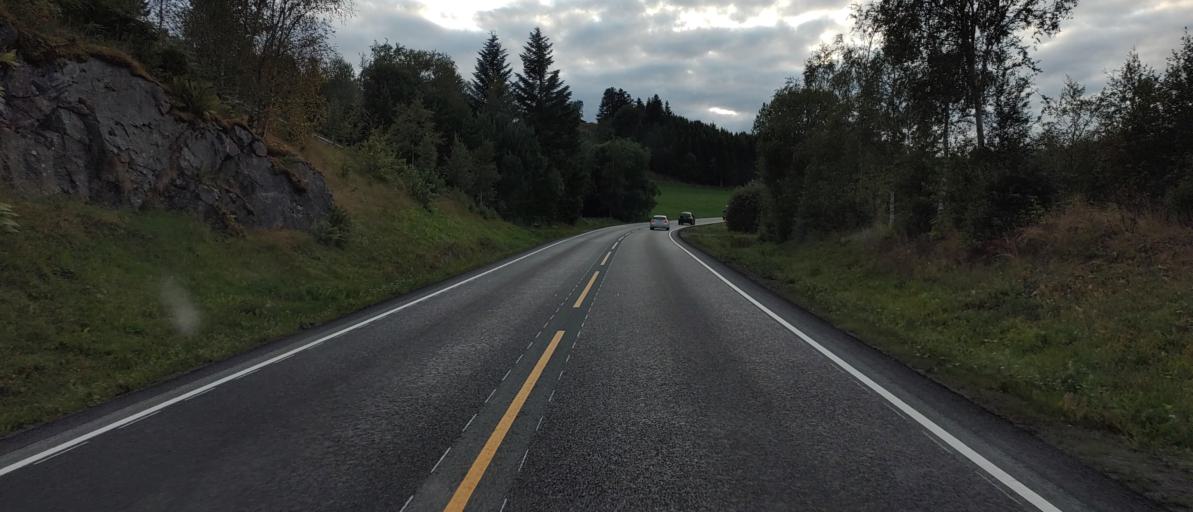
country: NO
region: More og Romsdal
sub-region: Molde
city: Hjelset
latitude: 62.7322
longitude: 7.3350
